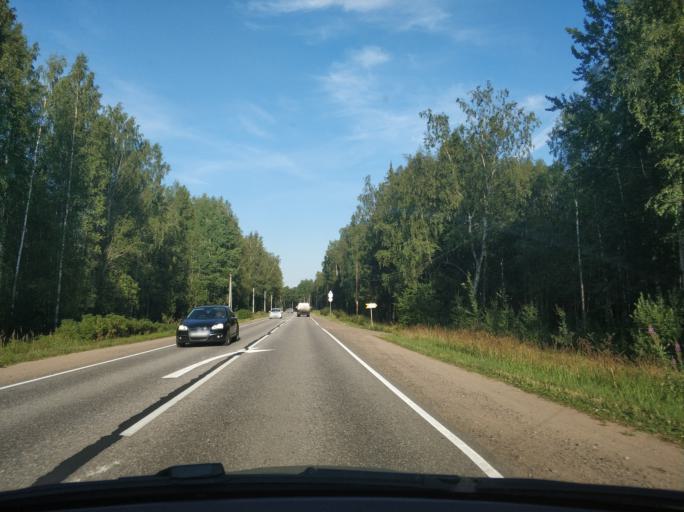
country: RU
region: Leningrad
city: Borisova Griva
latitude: 60.0914
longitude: 31.0023
